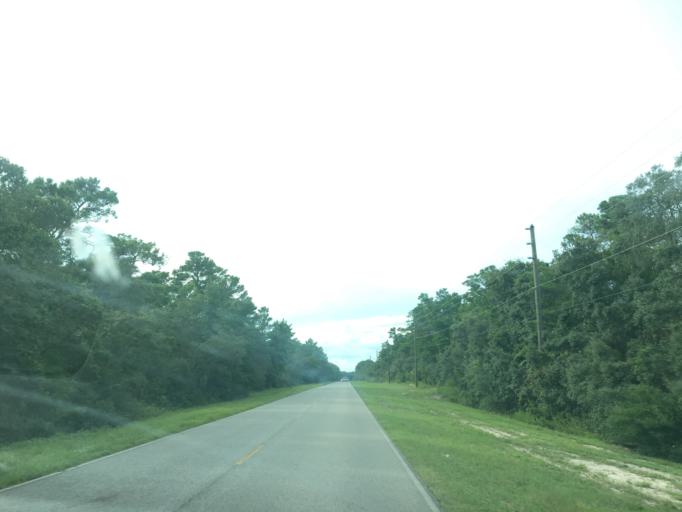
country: US
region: Florida
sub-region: Wakulla County
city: Crawfordville
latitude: 29.9189
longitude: -84.3709
